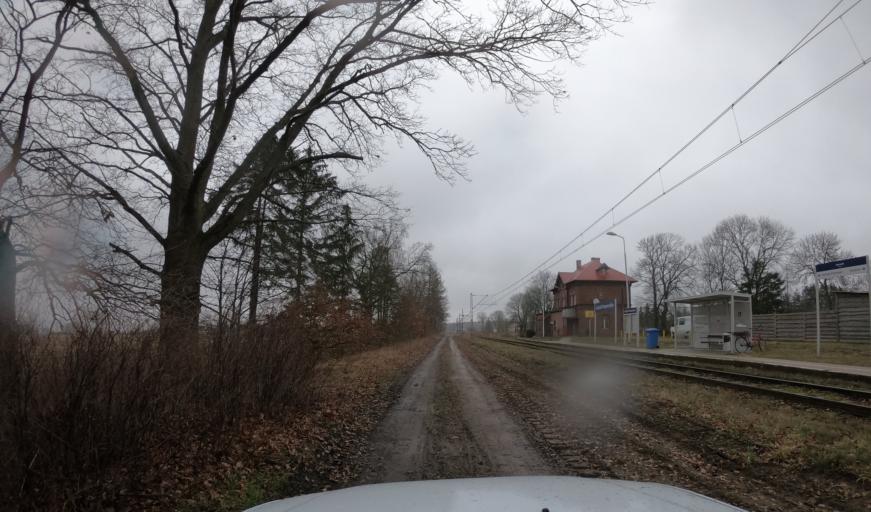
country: PL
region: West Pomeranian Voivodeship
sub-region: Powiat kamienski
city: Kamien Pomorski
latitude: 53.8986
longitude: 14.8243
